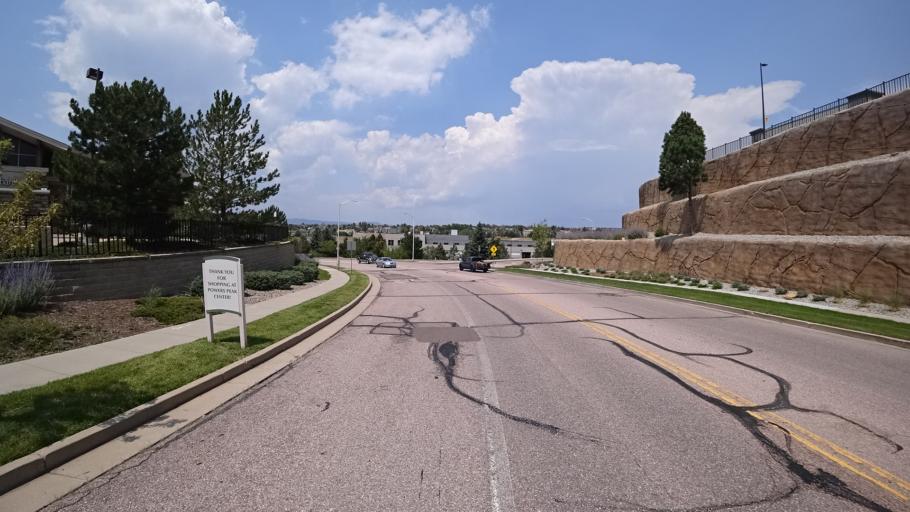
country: US
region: Colorado
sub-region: El Paso County
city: Black Forest
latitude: 38.9419
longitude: -104.7267
